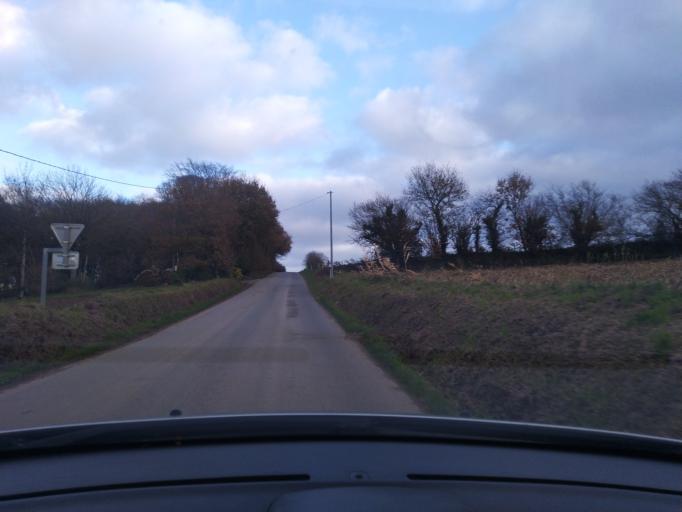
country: FR
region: Brittany
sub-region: Departement du Finistere
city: Plouigneau
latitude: 48.5672
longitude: -3.6710
